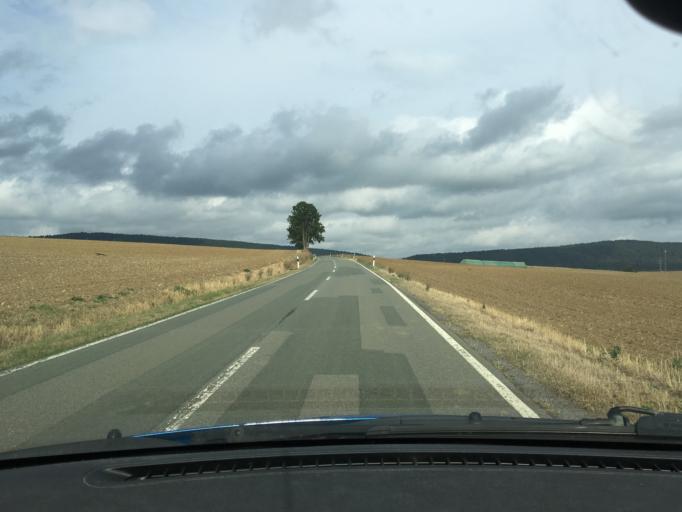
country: DE
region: Lower Saxony
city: Barsinghausen
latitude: 52.2469
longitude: 9.4387
